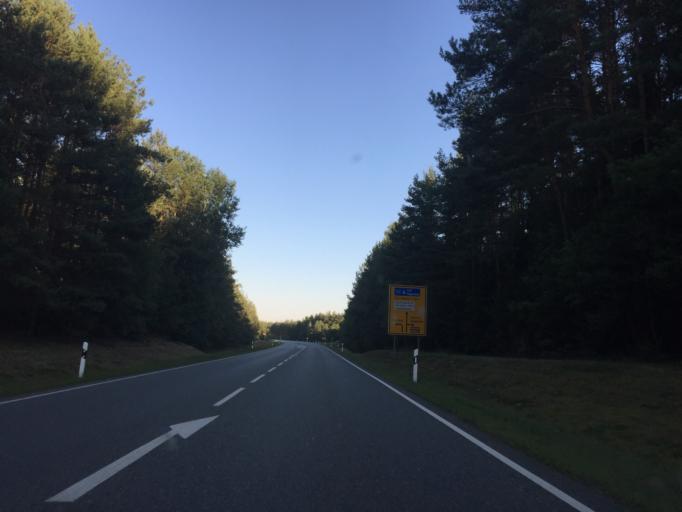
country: DE
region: Bavaria
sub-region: Upper Palatinate
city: Schwarzenbach
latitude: 49.7273
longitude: 11.9646
